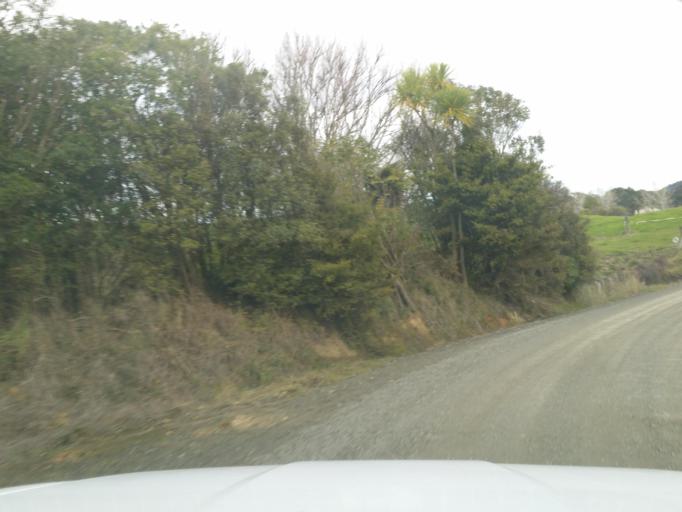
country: NZ
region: Northland
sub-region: Kaipara District
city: Dargaville
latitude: -35.8879
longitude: 173.9294
